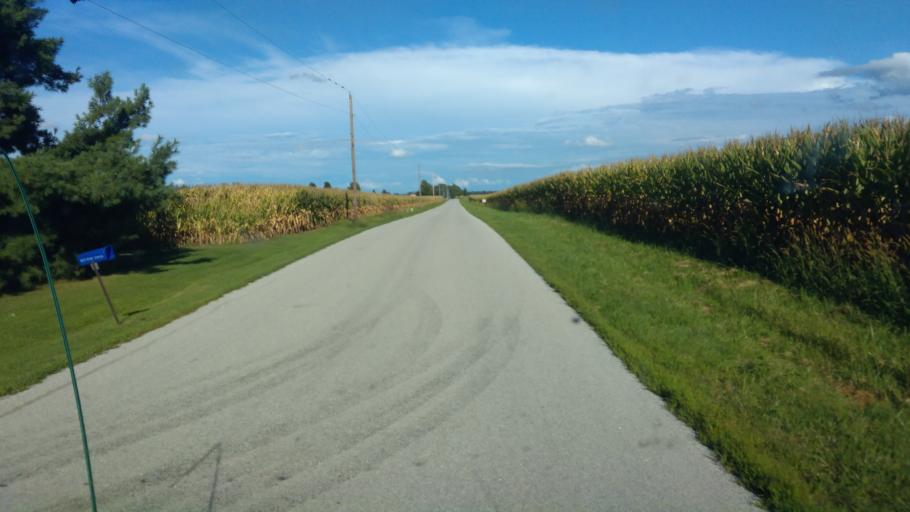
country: US
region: Ohio
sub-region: Hardin County
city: Ada
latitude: 40.7762
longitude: -83.6982
